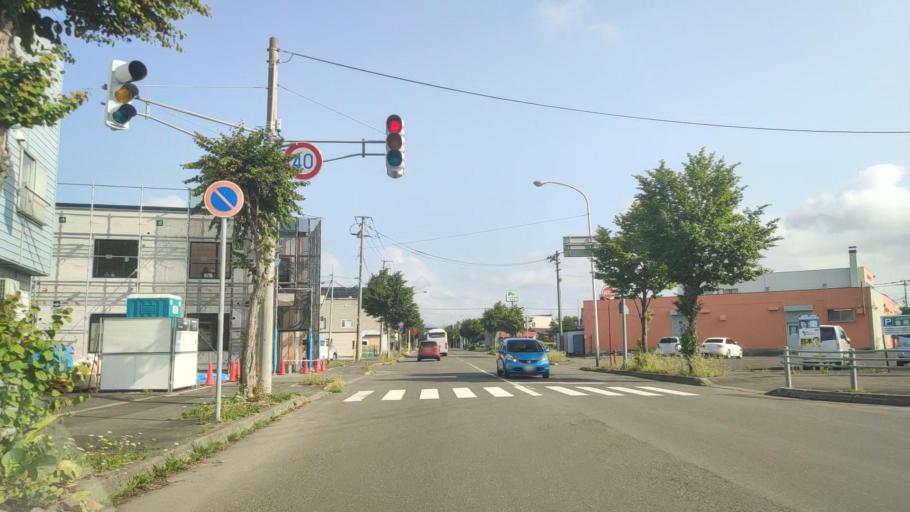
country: JP
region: Hokkaido
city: Shimo-furano
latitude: 43.3422
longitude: 142.3955
